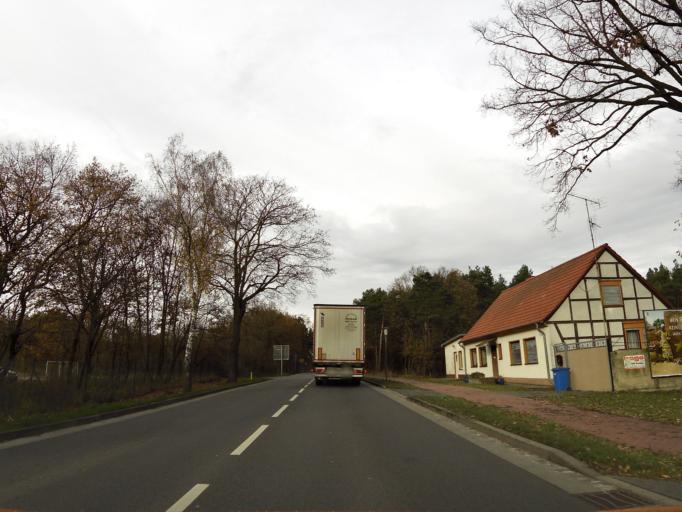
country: DE
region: Saxony-Anhalt
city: Klotze
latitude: 52.7043
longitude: 11.2539
